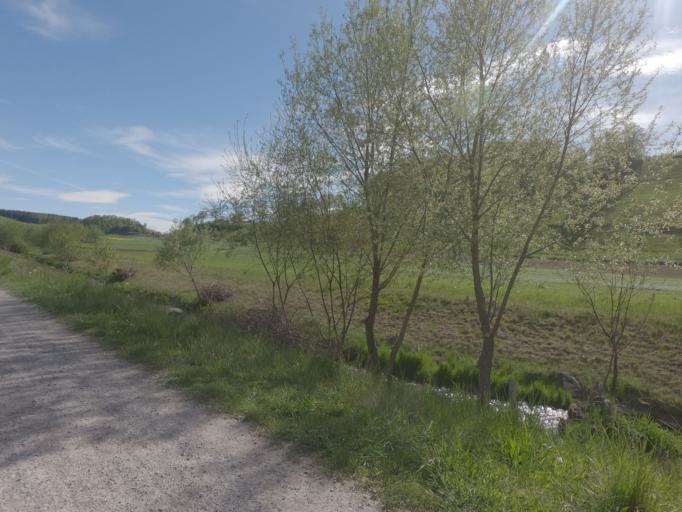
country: CH
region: Bern
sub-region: Bern-Mittelland District
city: Vechigen
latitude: 46.9383
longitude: 7.5515
